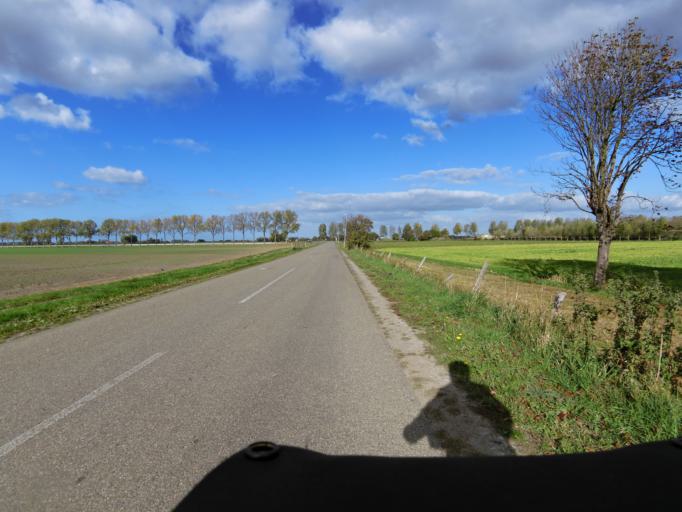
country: NL
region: North Brabant
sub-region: Gemeente Bergen op Zoom
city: Lepelstraat
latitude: 51.5655
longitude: 4.2674
